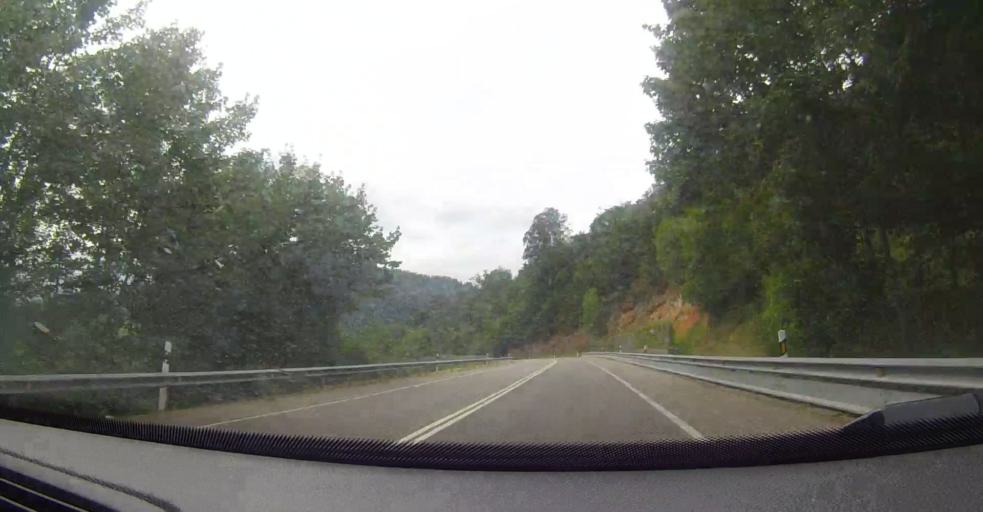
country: ES
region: Asturias
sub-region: Province of Asturias
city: Pilona
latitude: 43.3532
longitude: -5.3678
